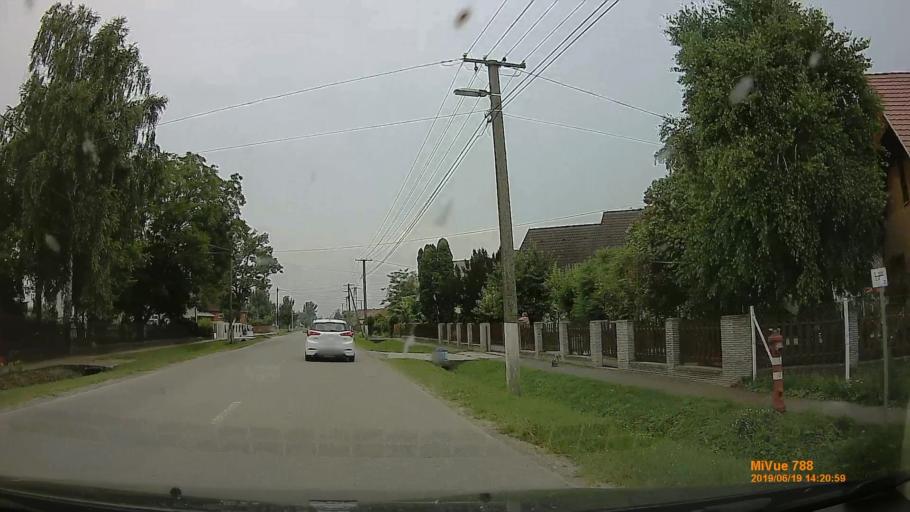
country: HU
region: Baranya
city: Szigetvar
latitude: 46.0219
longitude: 17.7749
